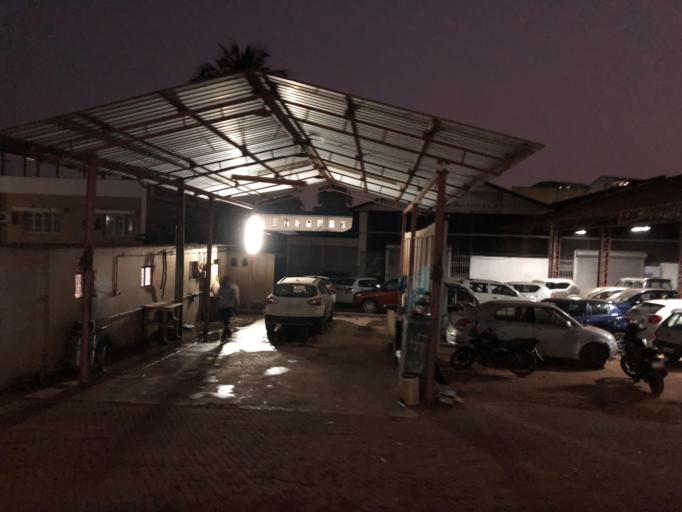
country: IN
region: Karnataka
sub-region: Dakshina Kannada
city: Mangalore
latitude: 12.8975
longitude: 74.8622
